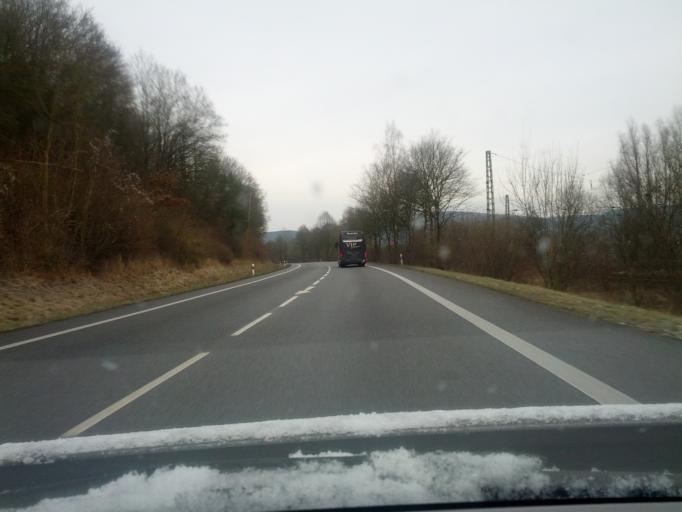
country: DE
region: Hesse
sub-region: Regierungsbezirk Kassel
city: Eschwege
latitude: 51.1945
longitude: 9.9961
